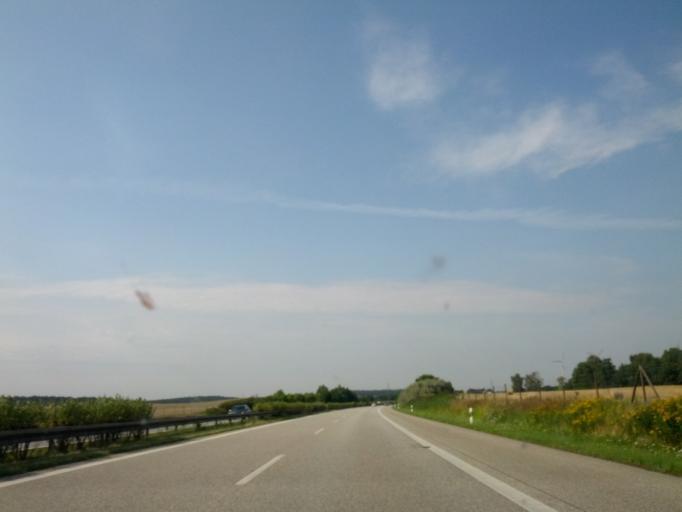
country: DE
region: Mecklenburg-Vorpommern
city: Muhl Rosin
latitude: 53.7993
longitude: 12.2997
